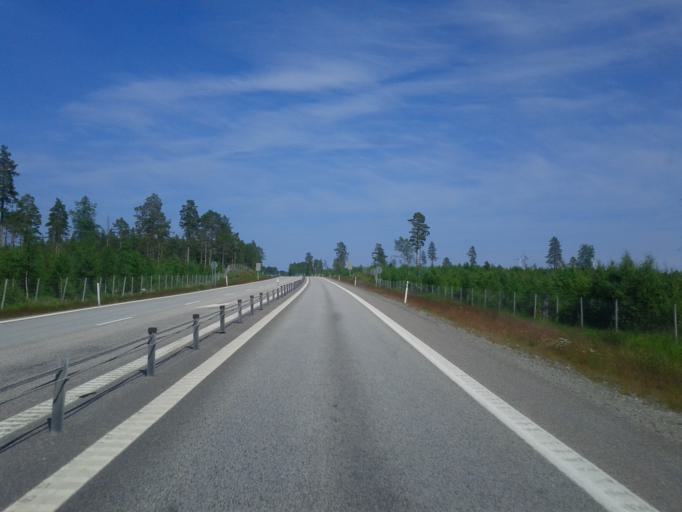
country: SE
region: Vaesterbotten
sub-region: Umea Kommun
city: Hoernefors
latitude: 63.6316
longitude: 19.8843
